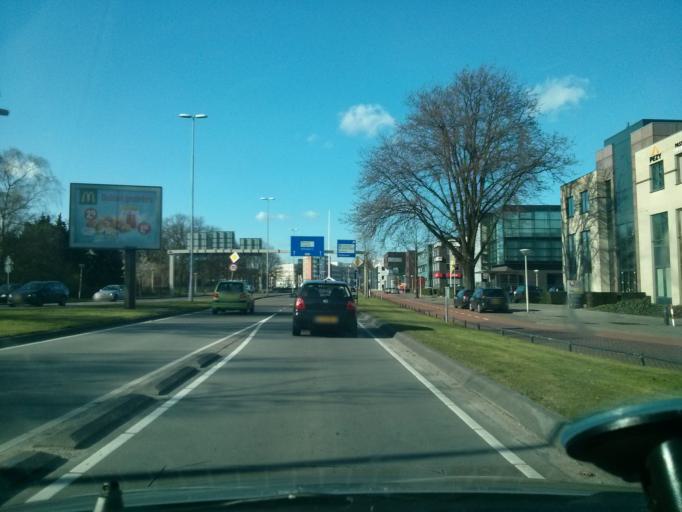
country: NL
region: North Brabant
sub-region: Gemeente Eindhoven
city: Eindhoven
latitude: 51.4419
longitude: 5.4497
